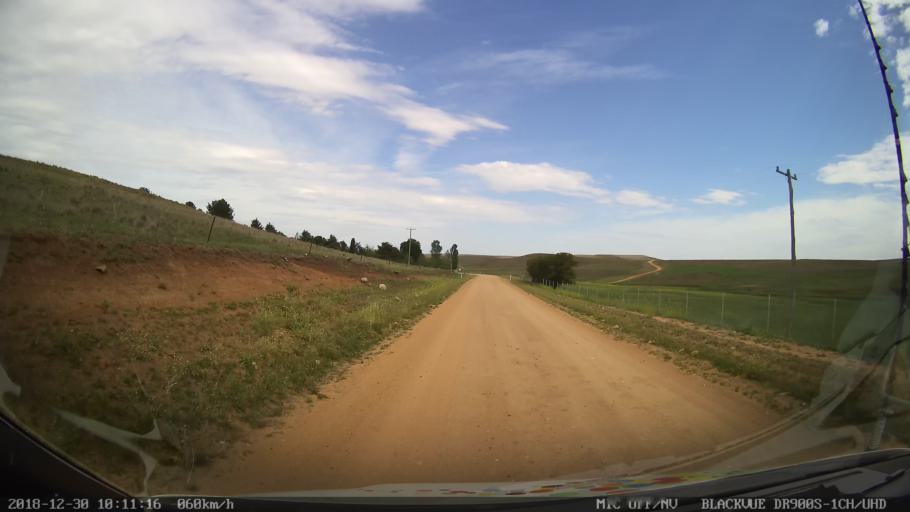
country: AU
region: New South Wales
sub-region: Cooma-Monaro
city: Cooma
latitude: -36.5482
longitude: 149.0866
